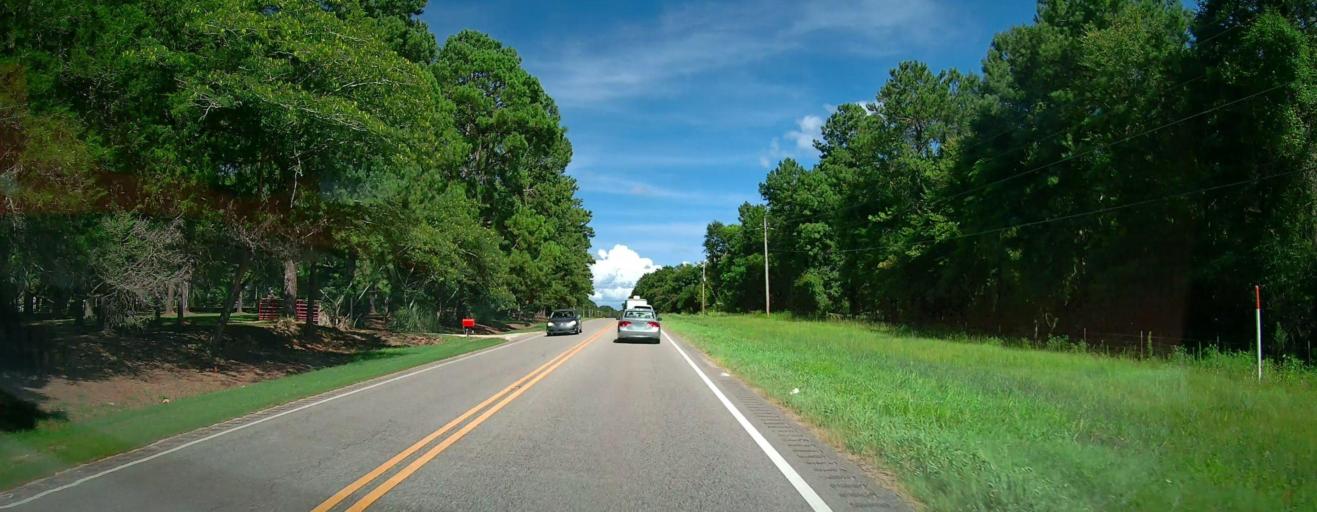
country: US
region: Alabama
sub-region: Elmore County
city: Tallassee
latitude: 32.3791
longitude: -85.8658
